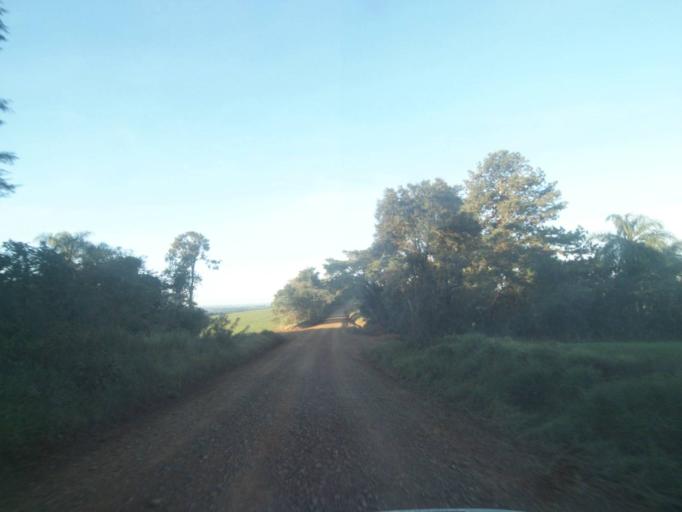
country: BR
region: Parana
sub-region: Tibagi
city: Tibagi
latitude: -24.5344
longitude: -50.5223
